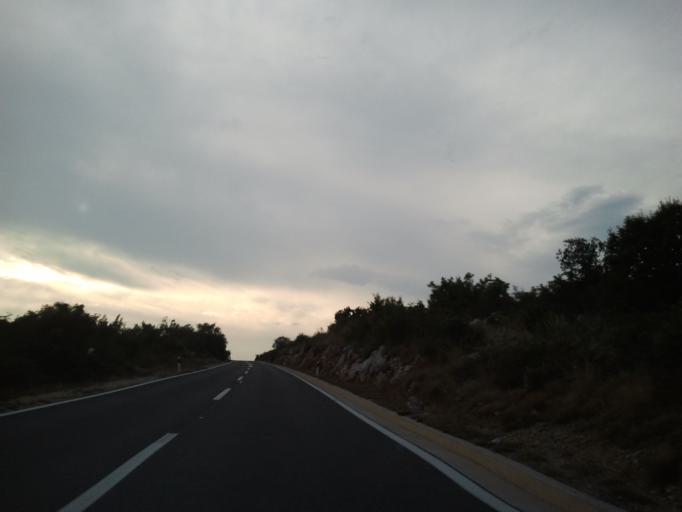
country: HR
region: Zadarska
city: Posedarje
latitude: 44.2250
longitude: 15.4390
